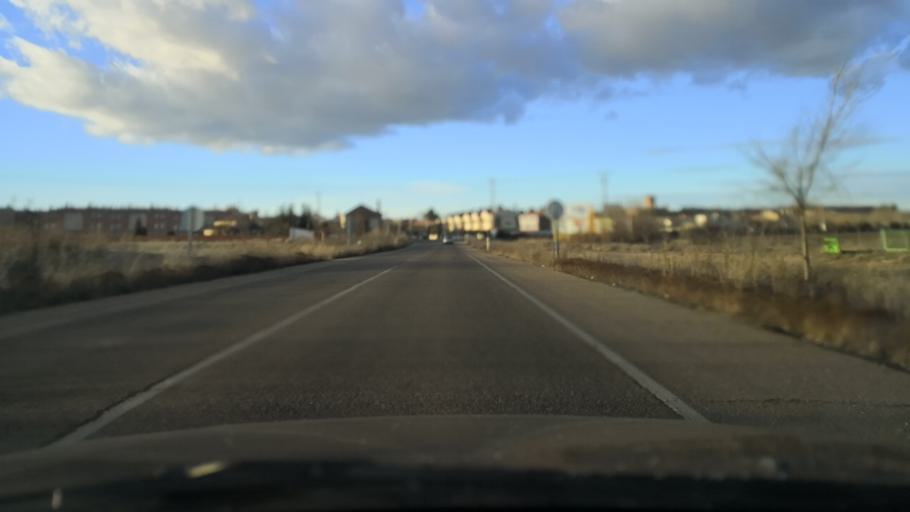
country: ES
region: Castille and Leon
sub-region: Provincia de Valladolid
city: Medina del Campo
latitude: 41.2980
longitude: -4.9051
